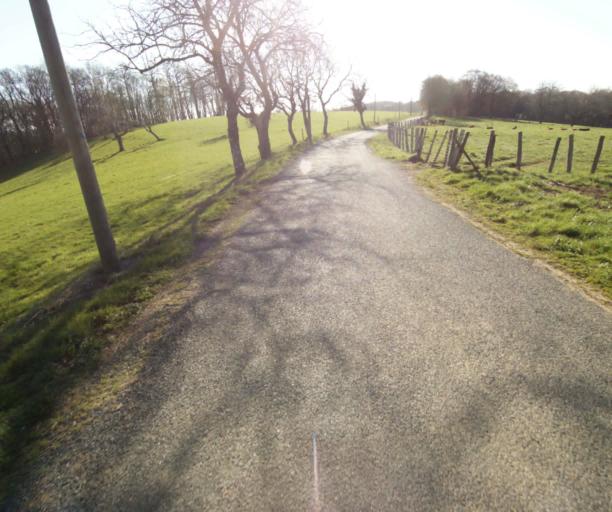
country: FR
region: Limousin
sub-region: Departement de la Correze
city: Seilhac
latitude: 45.3713
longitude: 1.7504
